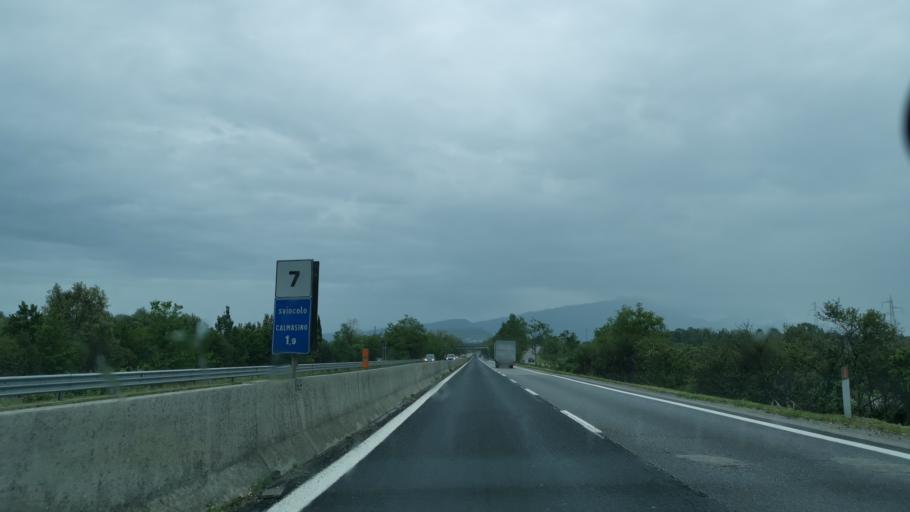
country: IT
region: Veneto
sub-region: Provincia di Verona
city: Calmasino
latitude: 45.4970
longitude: 10.7684
